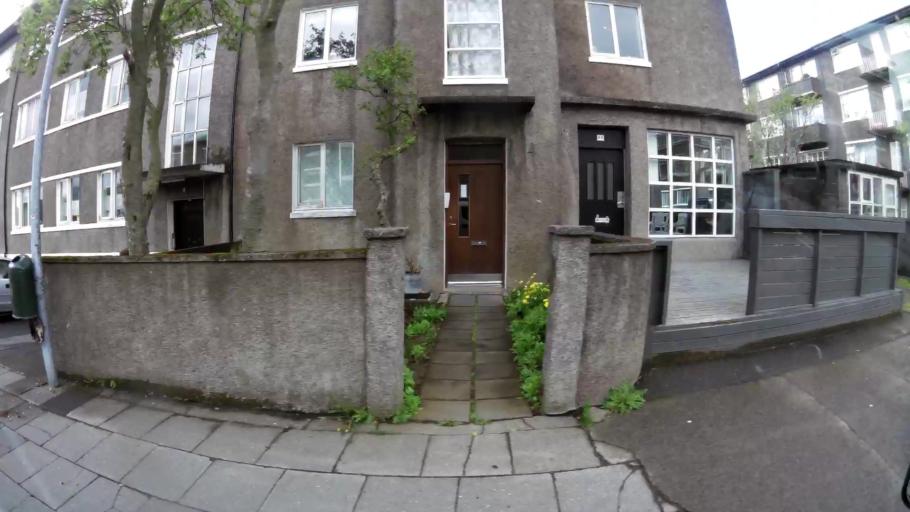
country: IS
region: Capital Region
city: Reykjavik
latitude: 64.1403
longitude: -21.9247
